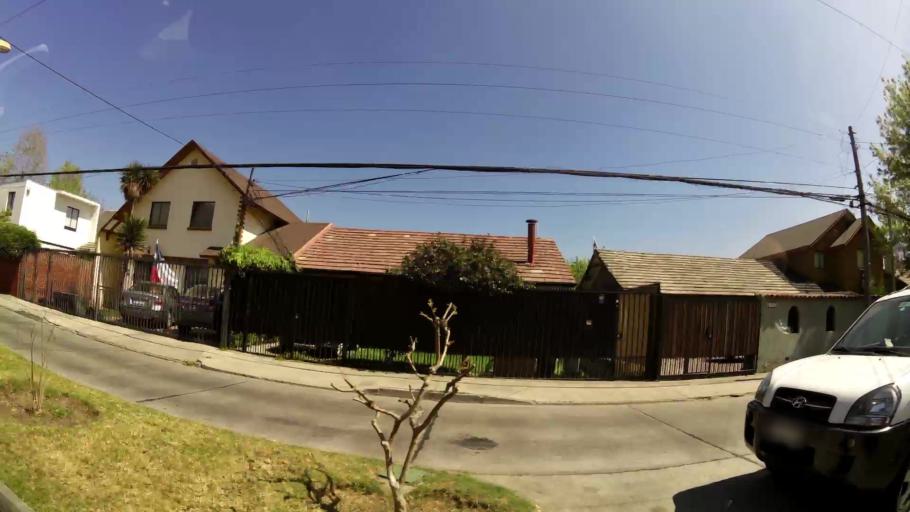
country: CL
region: Santiago Metropolitan
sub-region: Provincia de Santiago
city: Villa Presidente Frei, Nunoa, Santiago, Chile
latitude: -33.4276
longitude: -70.5458
